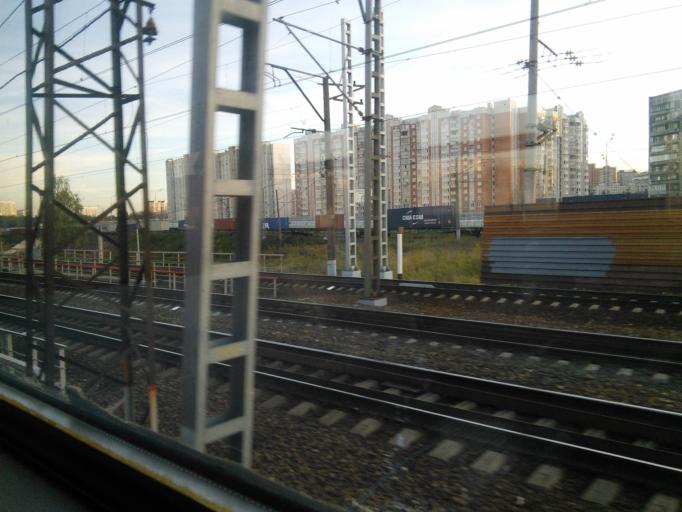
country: RU
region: Moscow
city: Novokhovrino
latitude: 55.8738
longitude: 37.5001
